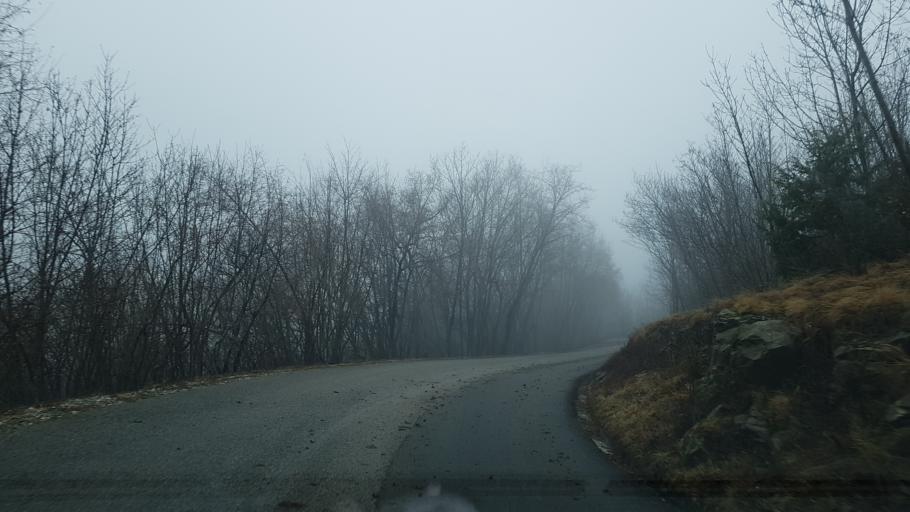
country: IT
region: Friuli Venezia Giulia
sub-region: Provincia di Udine
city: Stregna
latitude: 46.1133
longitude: 13.5861
